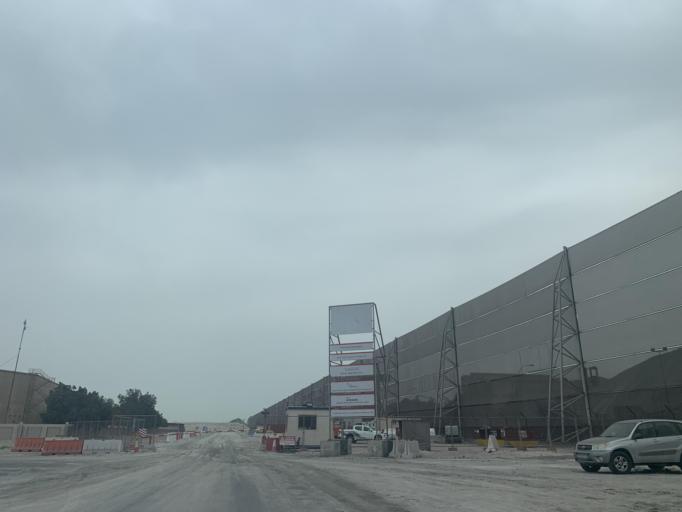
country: BH
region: Muharraq
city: Al Hadd
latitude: 26.2025
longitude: 50.6825
